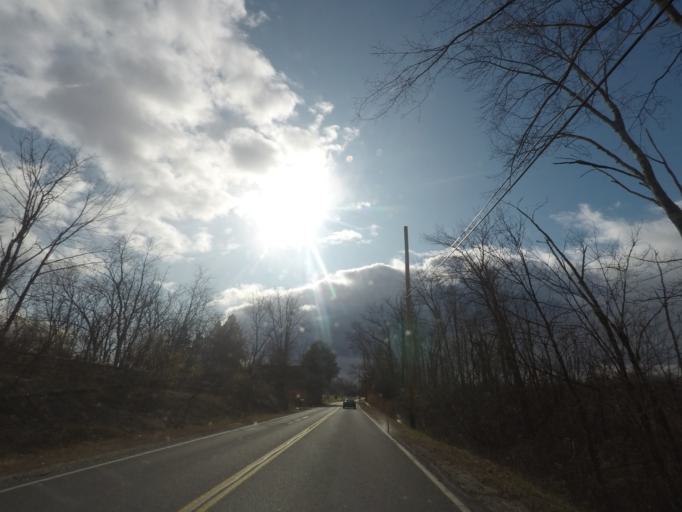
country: US
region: New York
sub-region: Saratoga County
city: Ballston Spa
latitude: 42.9467
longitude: -73.8519
